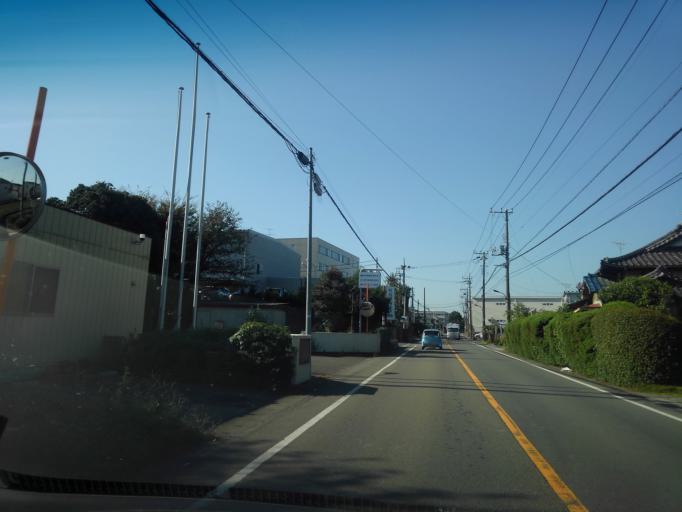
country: JP
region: Tokyo
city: Fussa
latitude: 35.7822
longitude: 139.3579
